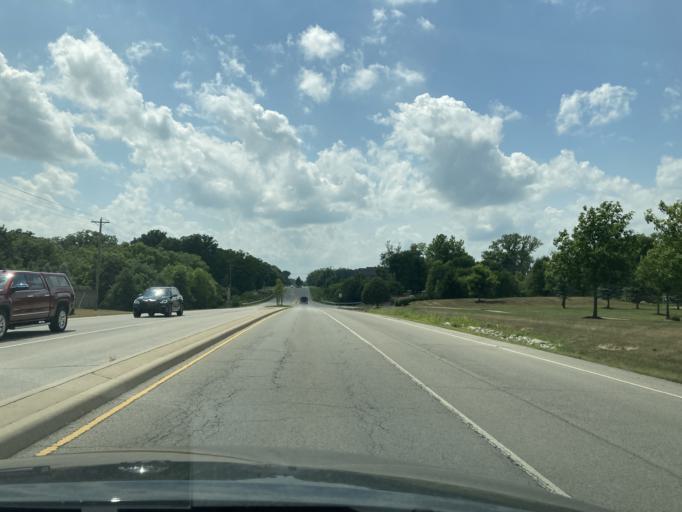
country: US
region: Indiana
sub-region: Boone County
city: Zionsville
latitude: 39.9987
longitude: -86.2480
